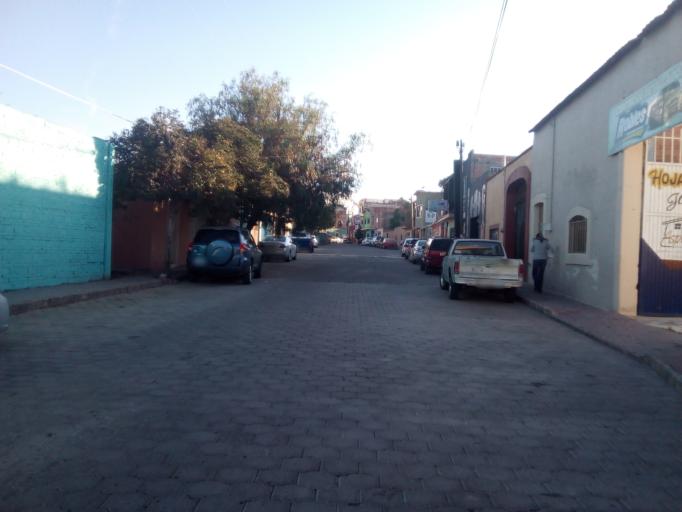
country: MX
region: Guerrero
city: San Luis de la Paz
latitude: 21.2953
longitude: -100.5161
